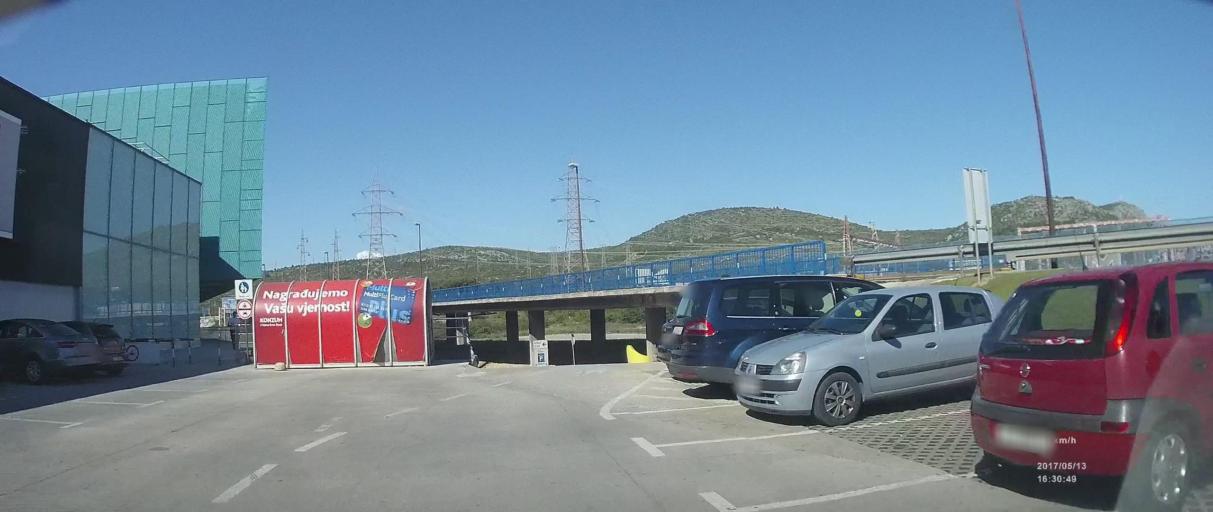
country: HR
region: Sibensko-Kniniska
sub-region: Grad Sibenik
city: Sibenik
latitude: 43.7120
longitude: 15.9133
